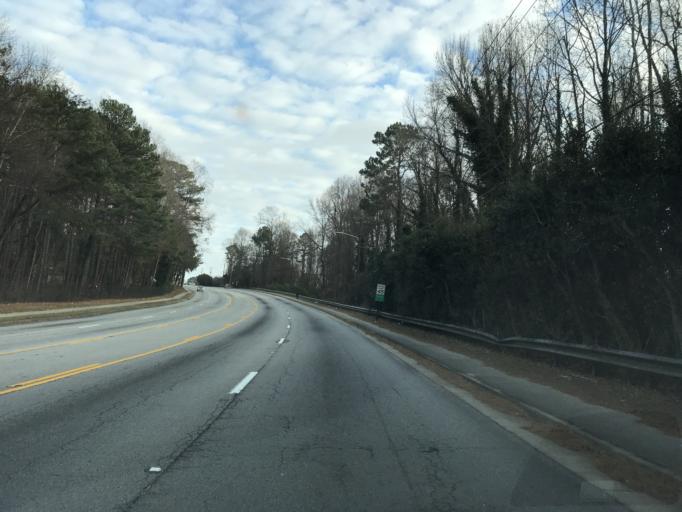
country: US
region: Georgia
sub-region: DeKalb County
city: Tucker
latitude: 33.8862
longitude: -84.2244
